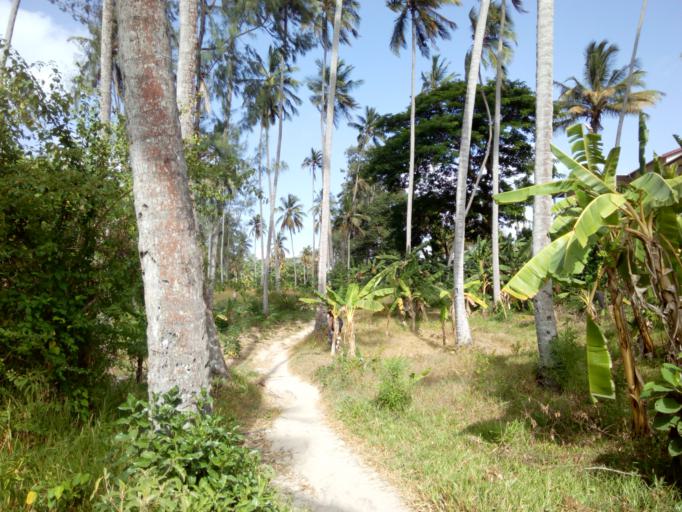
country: TZ
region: Zanzibar Urban/West
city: Zanzibar
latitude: -6.1809
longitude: 39.2017
